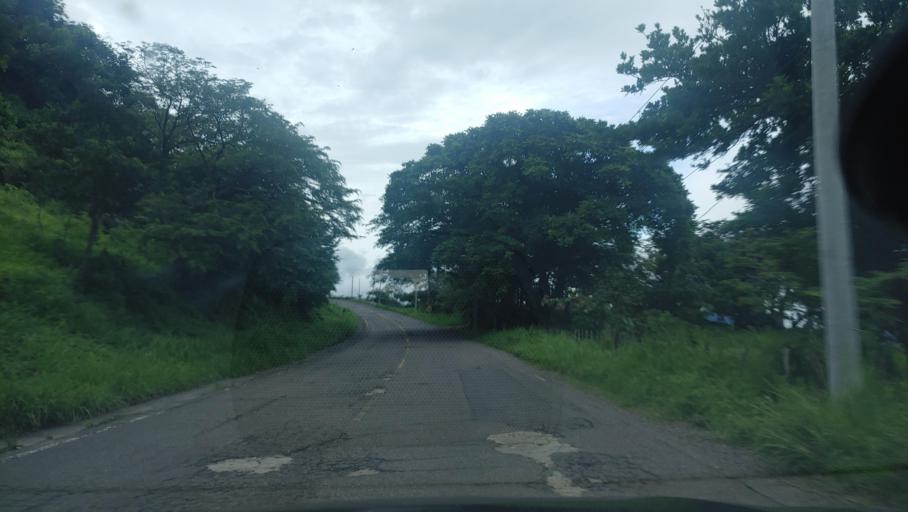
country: HN
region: Choluteca
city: Corpus
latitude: 13.3591
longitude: -86.9847
